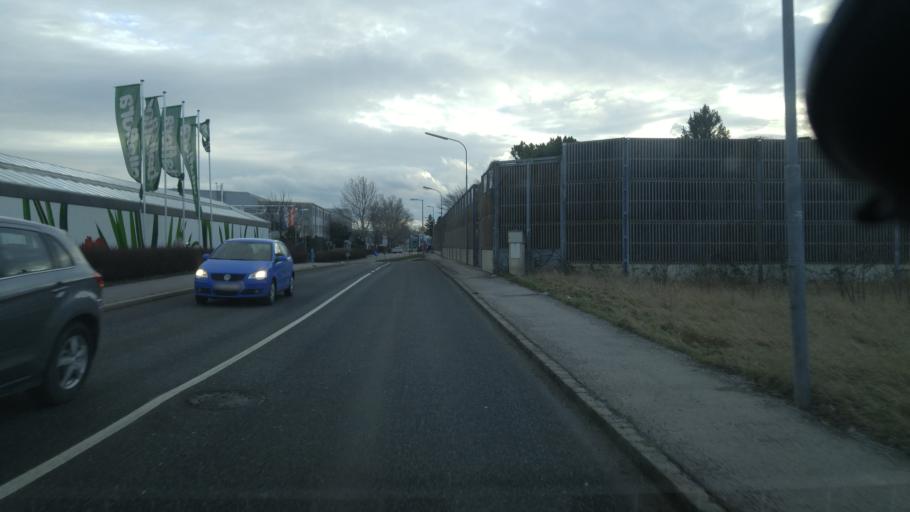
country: AT
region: Lower Austria
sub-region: Politischer Bezirk Baden
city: Bad Voslau
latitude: 47.9759
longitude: 16.2216
